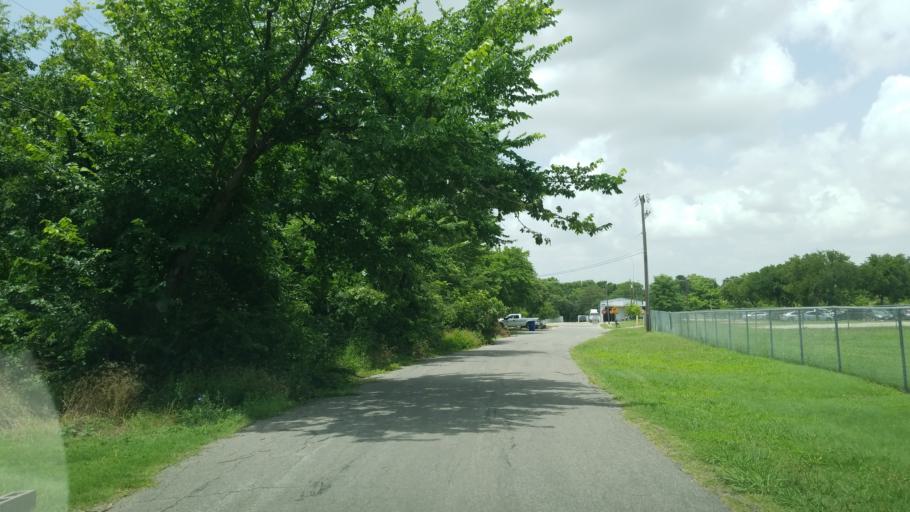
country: US
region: Texas
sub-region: Dallas County
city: Cockrell Hill
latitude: 32.7861
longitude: -96.8945
